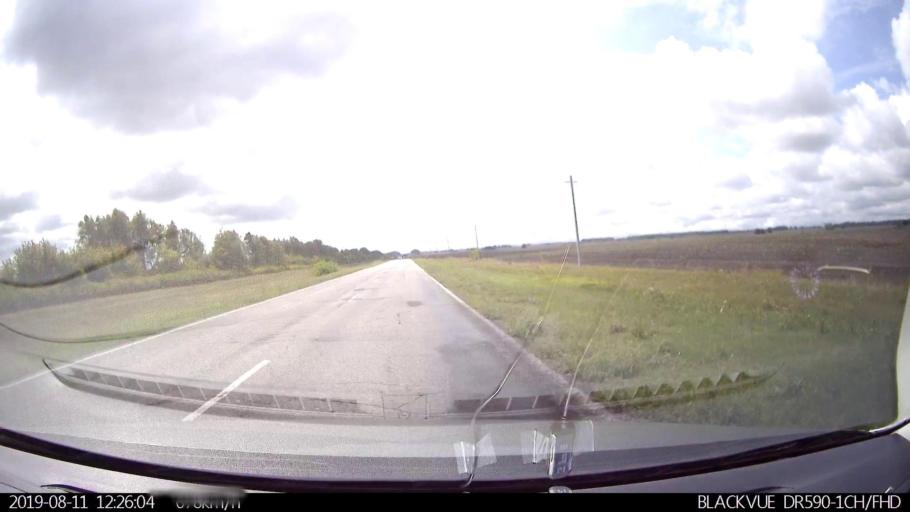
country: RU
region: Ulyanovsk
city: Ignatovka
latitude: 53.8676
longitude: 47.9342
